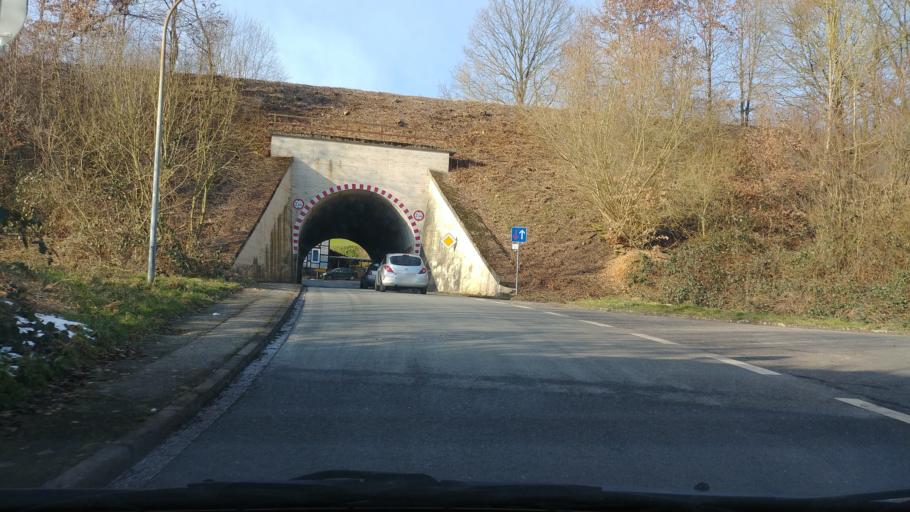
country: DE
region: Lower Saxony
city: Uslar
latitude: 51.6304
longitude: 9.6199
